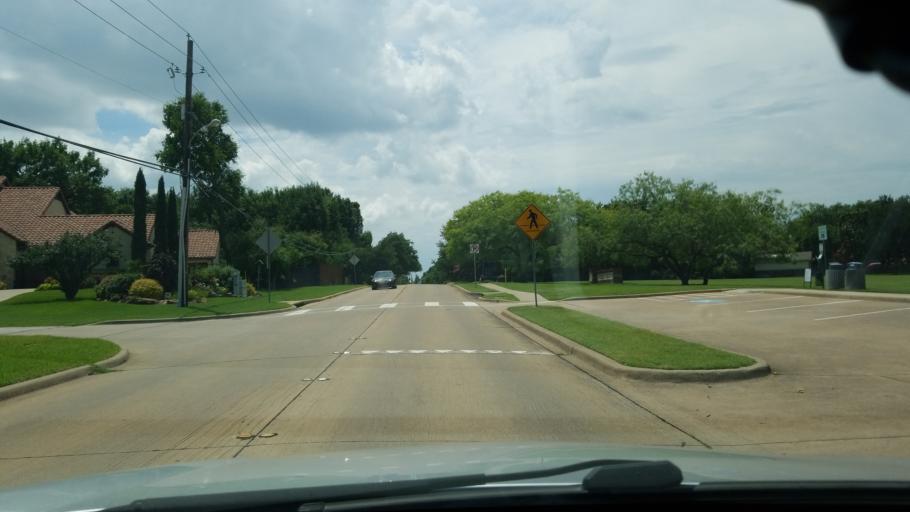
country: US
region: Texas
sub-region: Dallas County
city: Coppell
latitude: 32.9599
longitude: -96.9841
